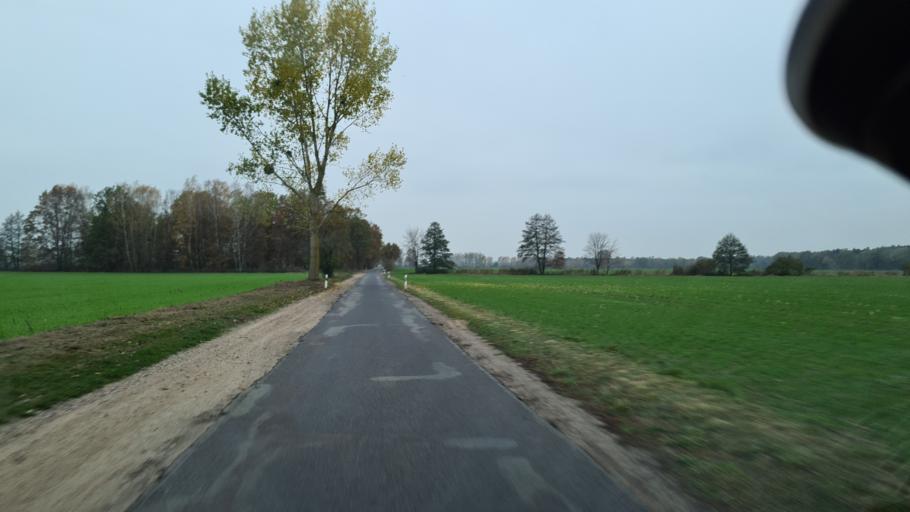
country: DE
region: Brandenburg
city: Lindow
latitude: 52.9285
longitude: 13.0070
